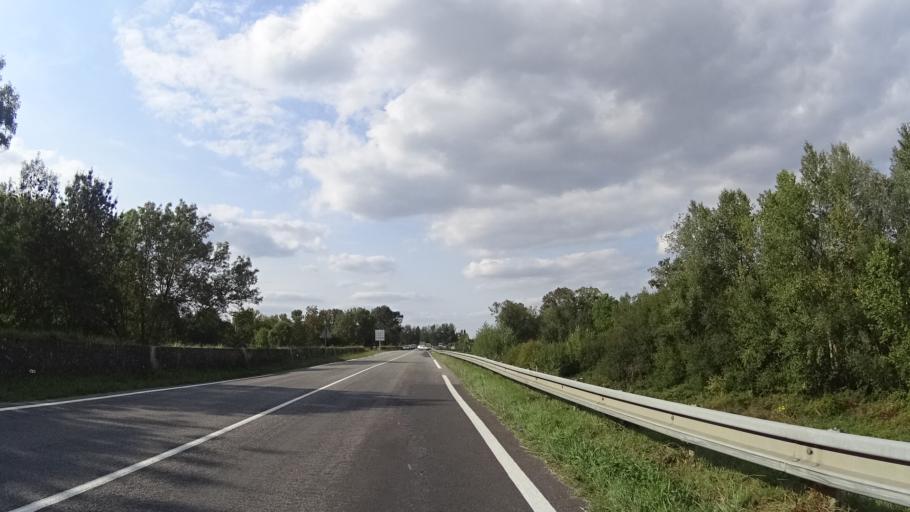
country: FR
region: Pays de la Loire
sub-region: Departement de Maine-et-Loire
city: Saint-Martin-de-la-Place
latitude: 47.3070
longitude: -0.1348
